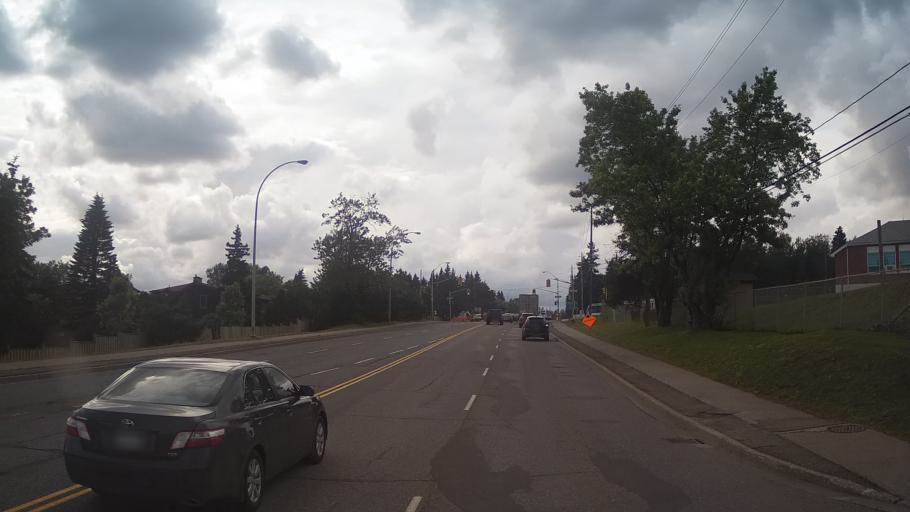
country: CA
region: Ontario
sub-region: Thunder Bay District
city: Thunder Bay
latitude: 48.4531
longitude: -89.2579
